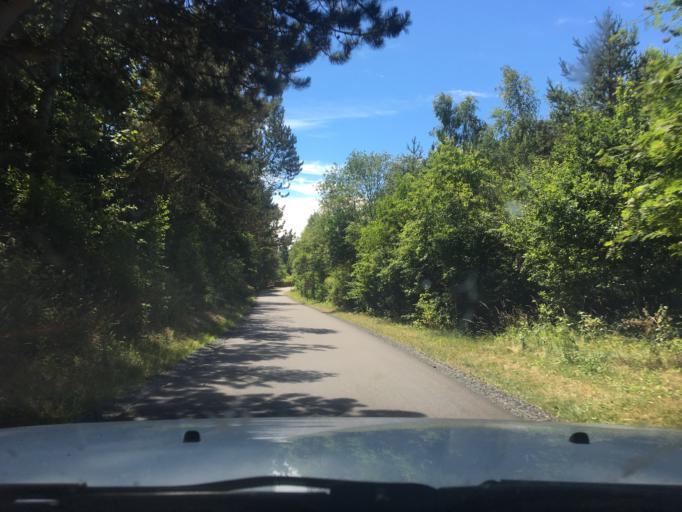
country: DK
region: Central Jutland
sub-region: Syddjurs Kommune
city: Ryomgard
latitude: 56.4171
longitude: 10.5639
